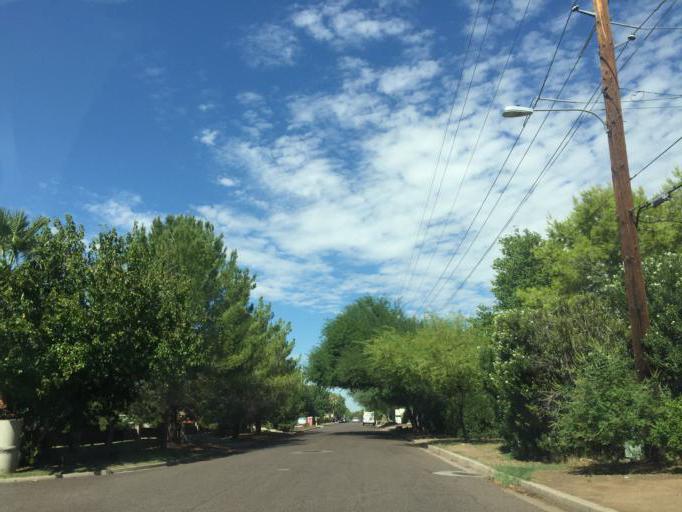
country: US
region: Arizona
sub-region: Maricopa County
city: Phoenix
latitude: 33.5347
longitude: -112.0517
